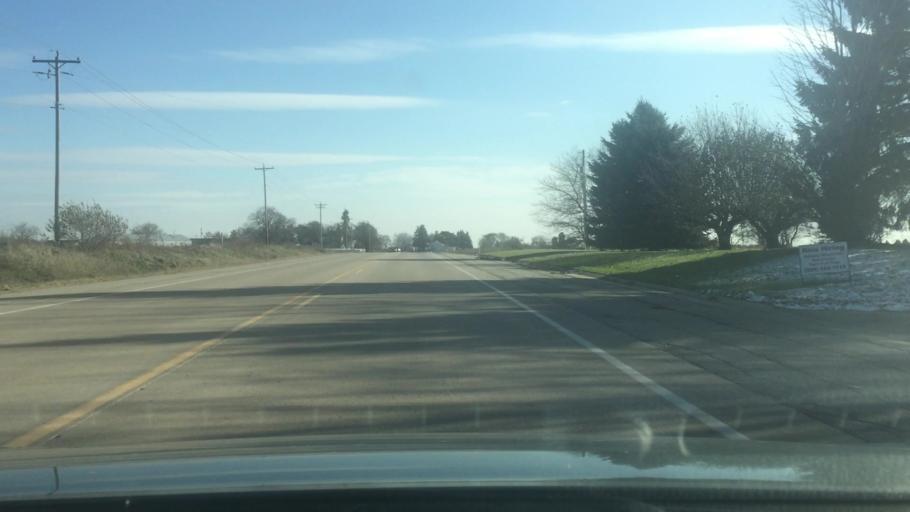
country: US
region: Wisconsin
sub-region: Jefferson County
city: Fort Atkinson
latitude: 42.9539
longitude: -88.8827
